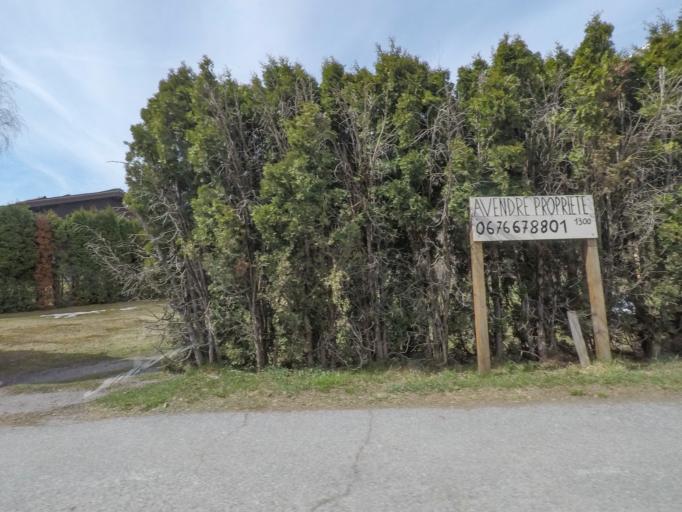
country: FR
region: Rhone-Alpes
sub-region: Departement de la Haute-Savoie
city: Chamonix-Mont-Blanc
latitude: 45.9397
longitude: 6.8879
